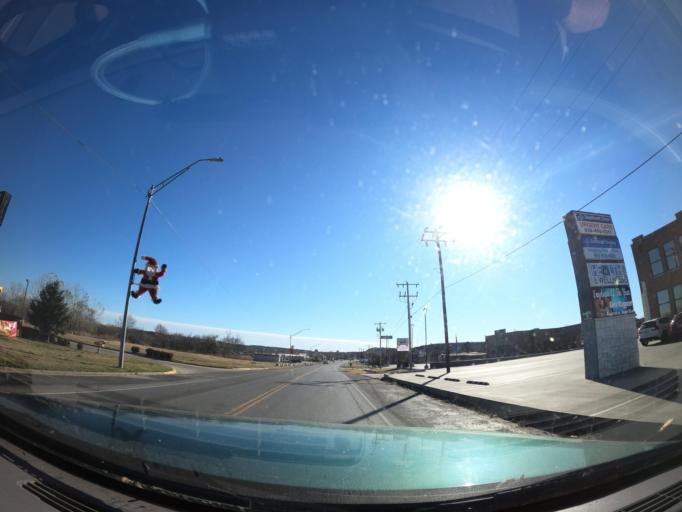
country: US
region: Oklahoma
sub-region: McIntosh County
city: Eufaula
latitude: 35.2822
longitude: -95.5828
